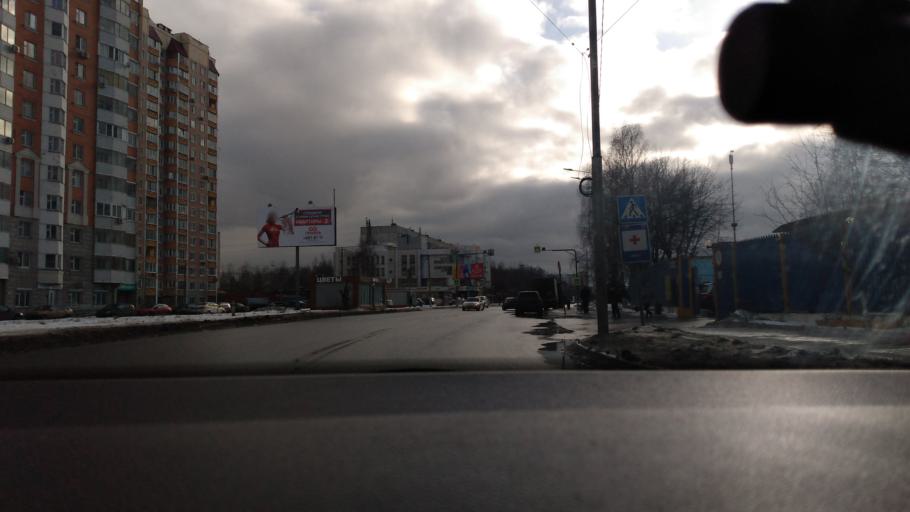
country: RU
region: Moskovskaya
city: Balashikha
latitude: 55.8281
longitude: 37.9547
